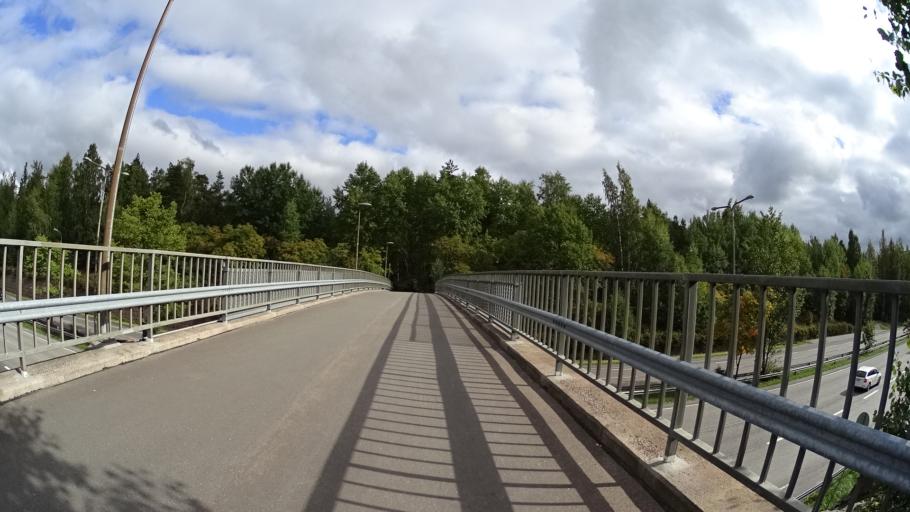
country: FI
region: Uusimaa
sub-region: Helsinki
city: Helsinki
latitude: 60.2329
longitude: 24.9017
